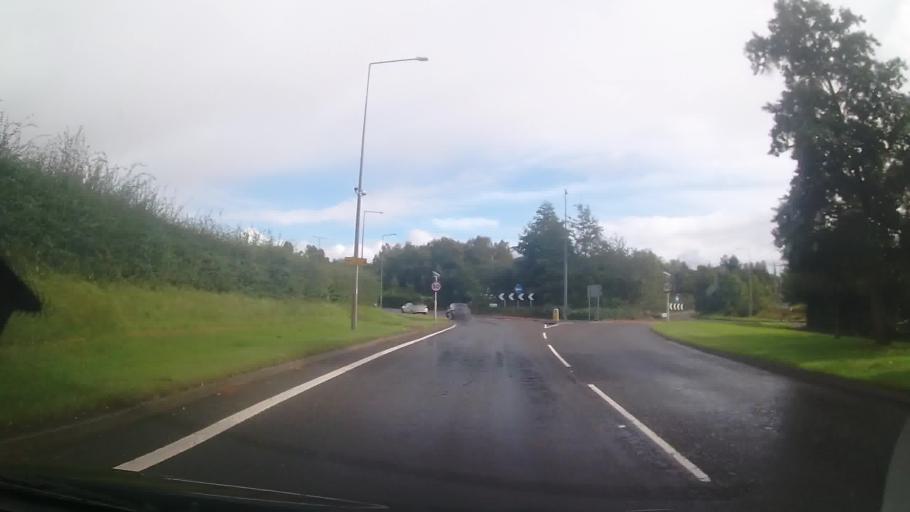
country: GB
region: England
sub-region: Telford and Wrekin
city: Ironbridge
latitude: 52.6522
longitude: -2.4965
